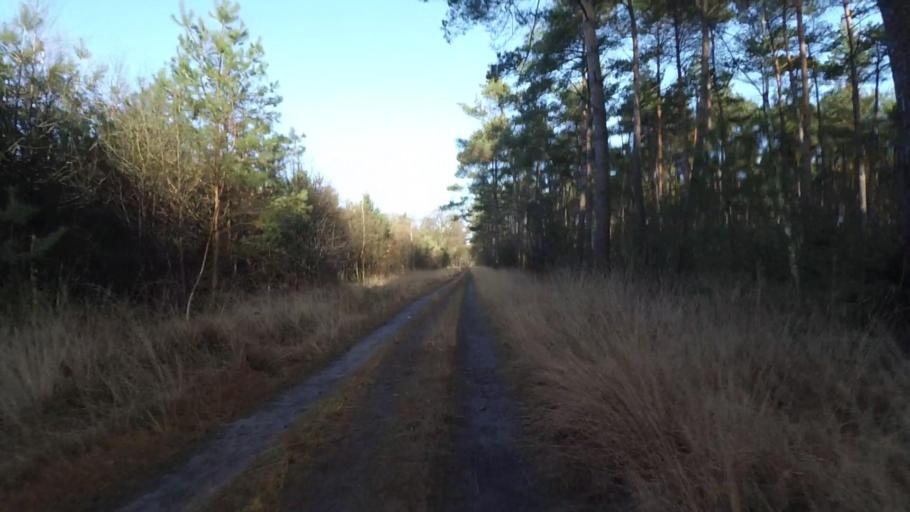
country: NL
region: Utrecht
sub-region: Gemeente Utrechtse Heuvelrug
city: Maarn
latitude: 52.1059
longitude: 5.3719
